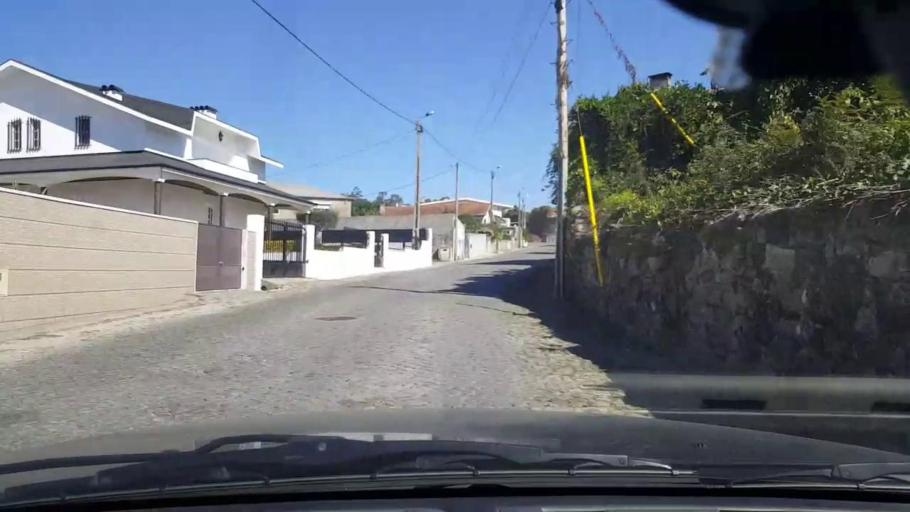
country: PT
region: Porto
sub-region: Maia
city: Gemunde
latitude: 41.3063
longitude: -8.6580
